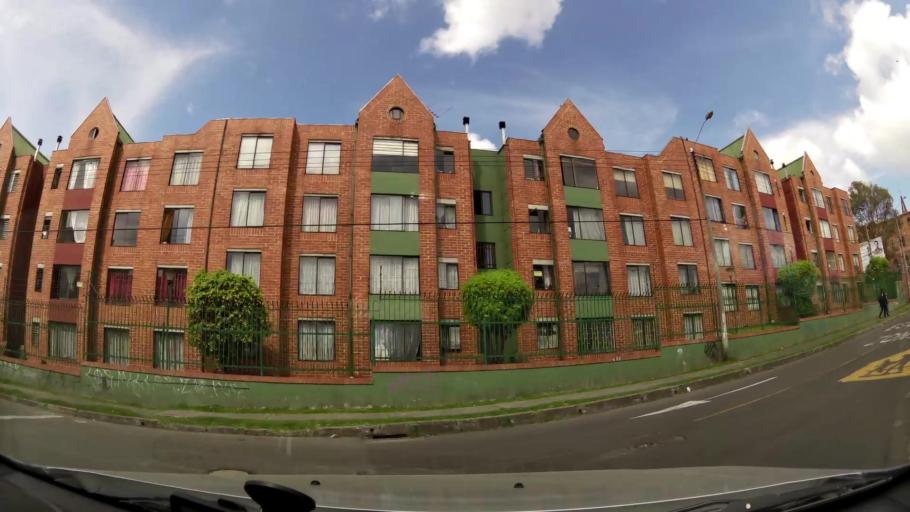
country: CO
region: Bogota D.C.
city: Bogota
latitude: 4.5693
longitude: -74.0965
